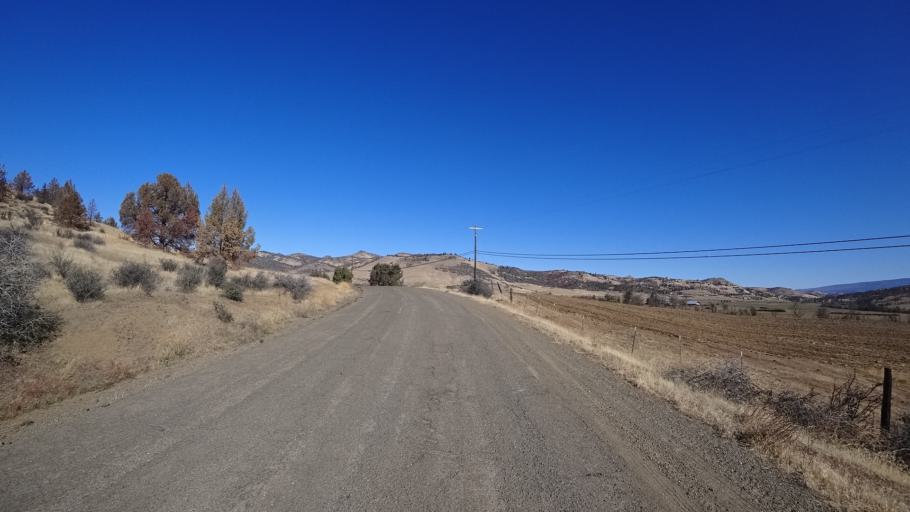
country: US
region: California
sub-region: Siskiyou County
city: Montague
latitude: 41.8905
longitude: -122.5499
